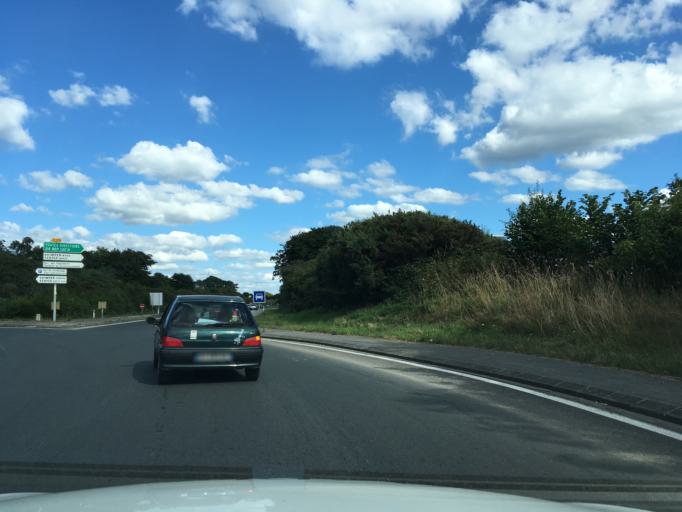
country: FR
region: Brittany
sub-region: Departement du Finistere
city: Pluguffan
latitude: 48.0014
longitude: -4.1574
